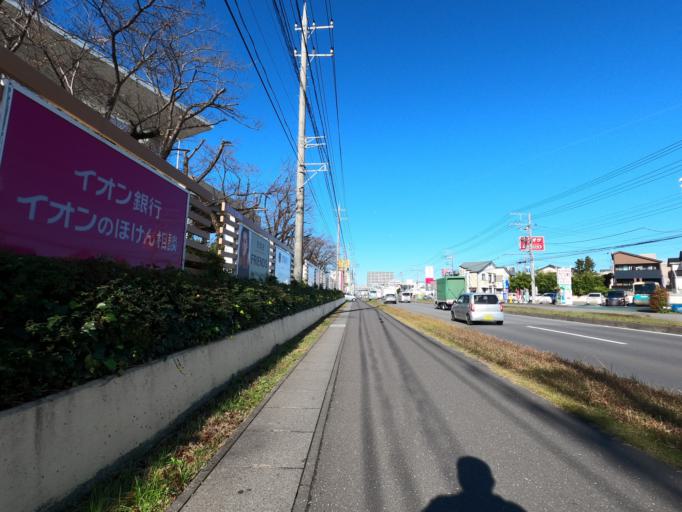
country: JP
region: Ibaraki
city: Moriya
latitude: 35.9448
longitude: 139.9928
